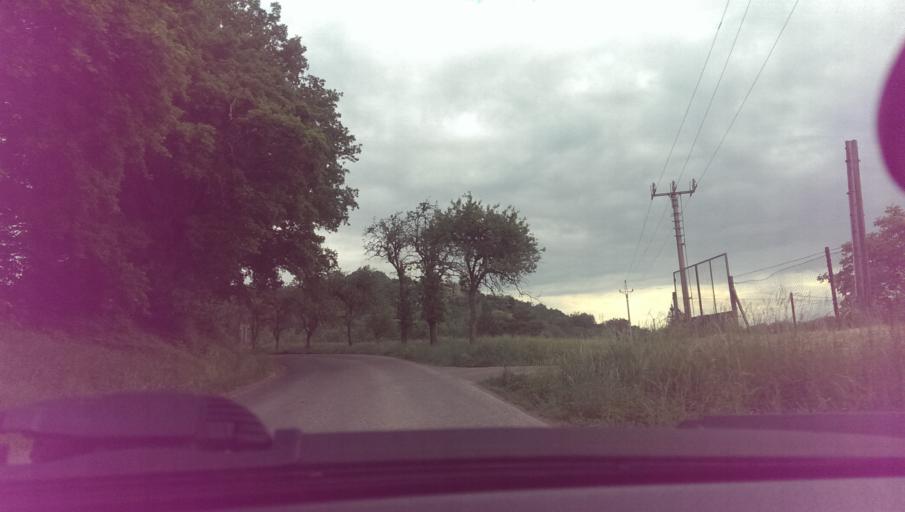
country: CZ
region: Zlin
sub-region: Okres Zlin
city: Napajedla
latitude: 49.1859
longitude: 17.5052
